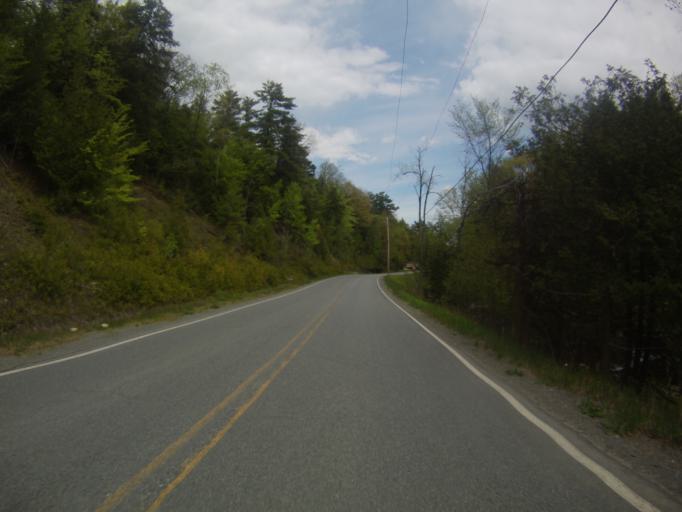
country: US
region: New York
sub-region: Essex County
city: Ticonderoga
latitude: 43.9421
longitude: -73.4758
